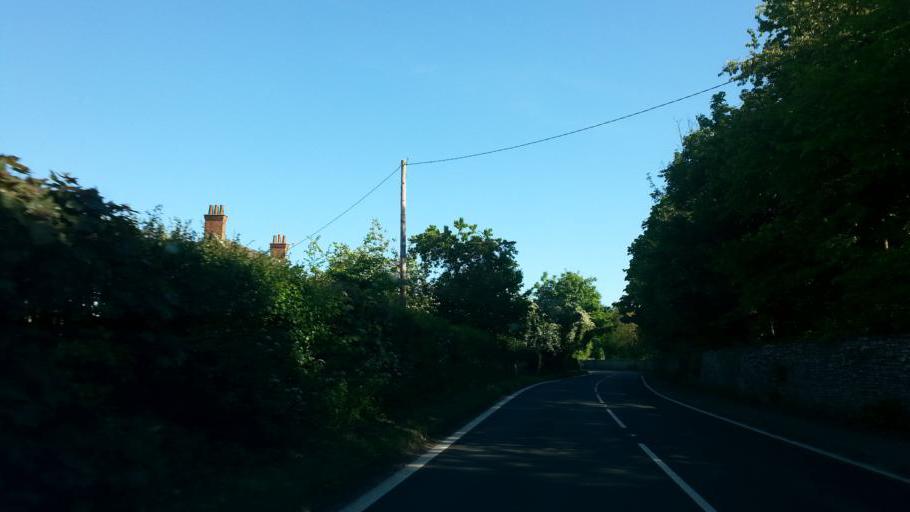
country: GB
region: England
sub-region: Dorset
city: Stalbridge
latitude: 50.9701
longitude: -2.3877
